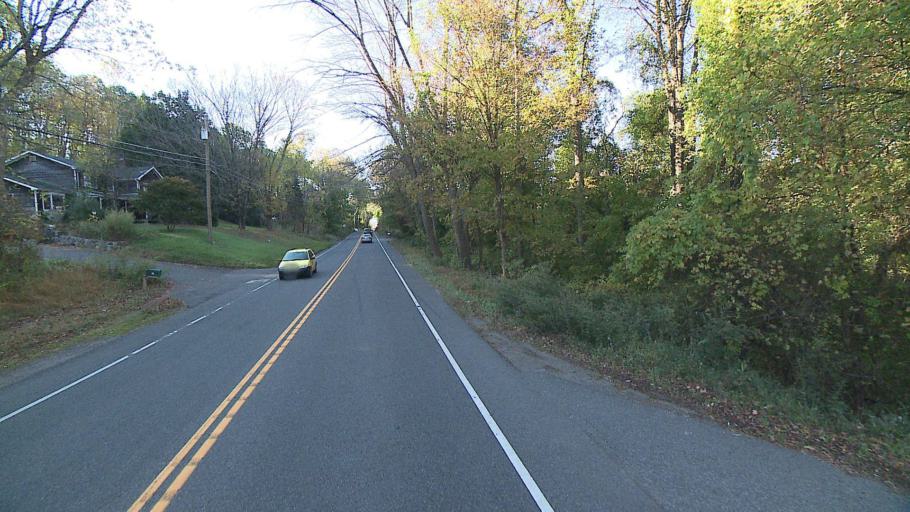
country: US
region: Connecticut
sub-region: Fairfield County
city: Bethel
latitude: 41.3411
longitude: -73.4153
